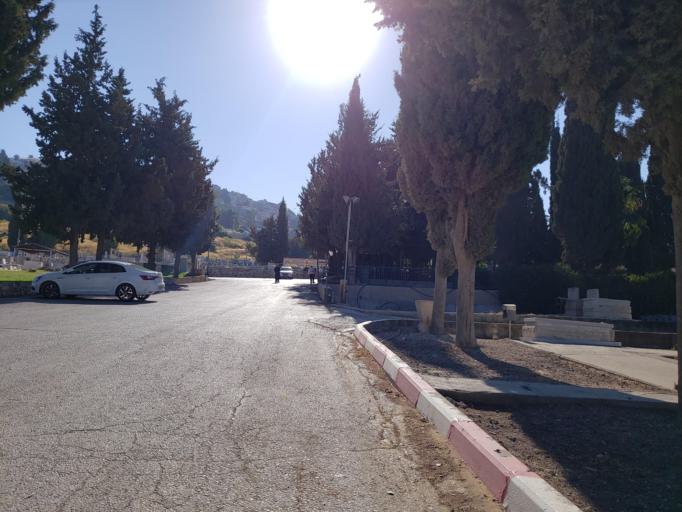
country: IL
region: Northern District
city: Safed
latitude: 32.9679
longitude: 35.4861
